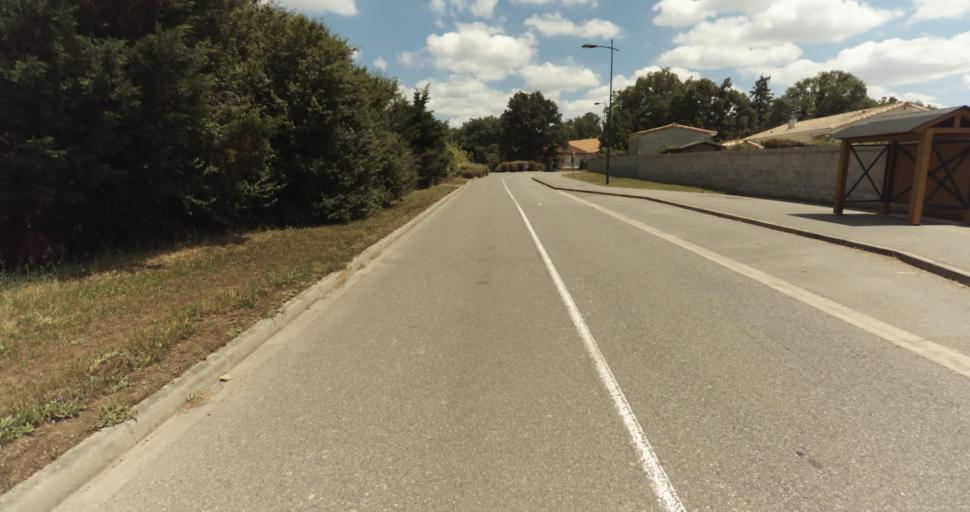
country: FR
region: Midi-Pyrenees
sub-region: Departement de la Haute-Garonne
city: Fontenilles
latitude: 43.5369
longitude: 1.1911
